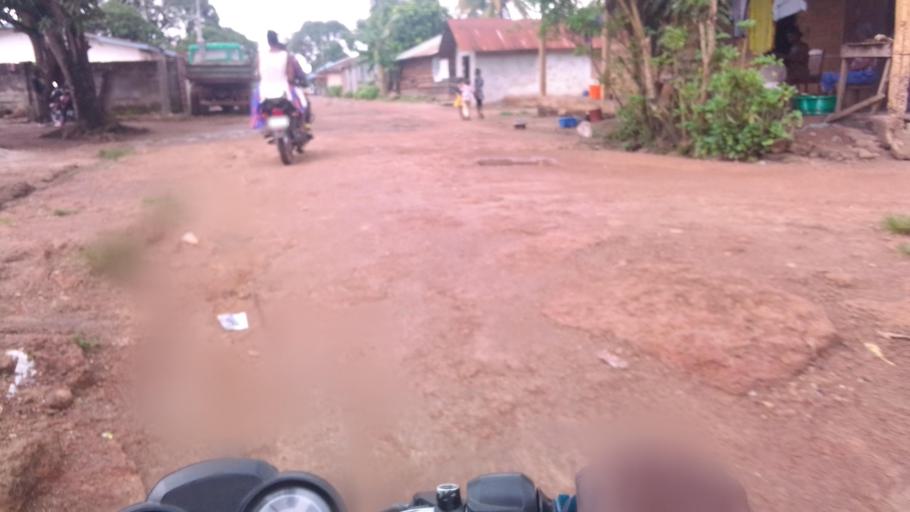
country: SL
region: Eastern Province
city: Kenema
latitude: 7.8857
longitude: -11.1830
